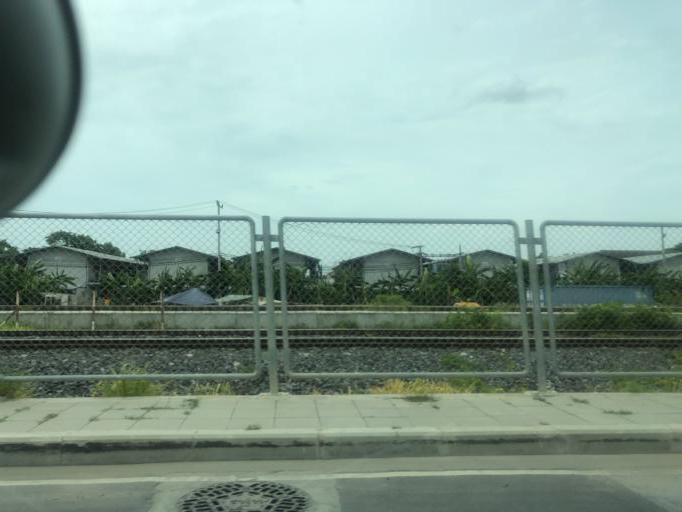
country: TH
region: Bangkok
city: Don Mueang
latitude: 13.9536
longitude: 100.6065
